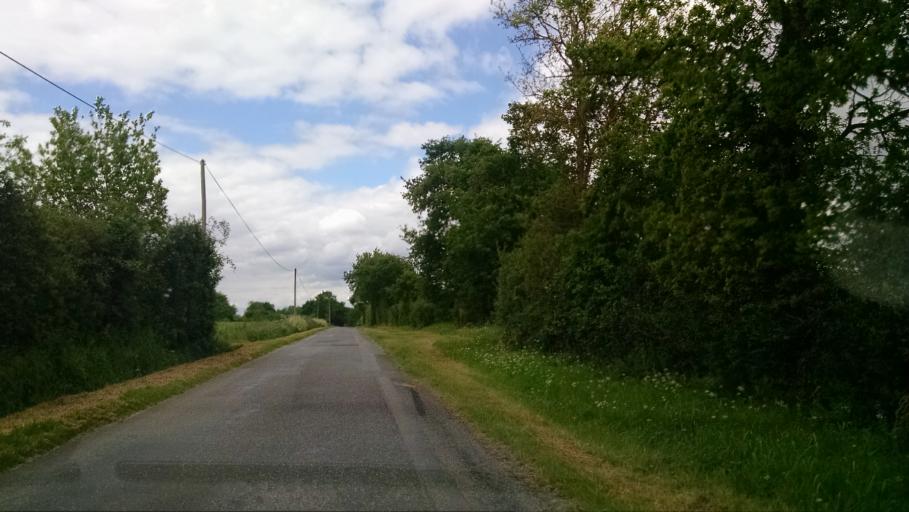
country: FR
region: Pays de la Loire
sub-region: Departement de la Loire-Atlantique
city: Remouille
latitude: 47.0279
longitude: -1.3830
